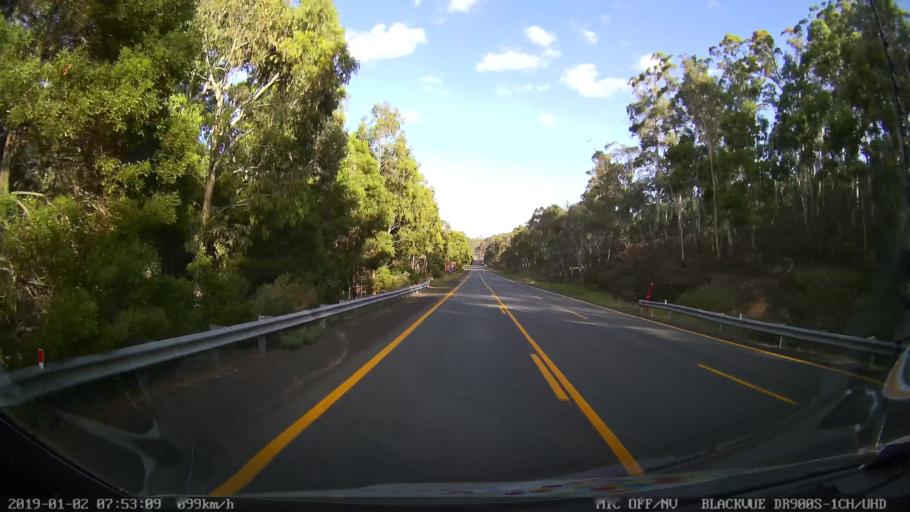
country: AU
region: New South Wales
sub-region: Tumut Shire
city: Tumut
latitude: -35.7087
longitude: 148.5100
